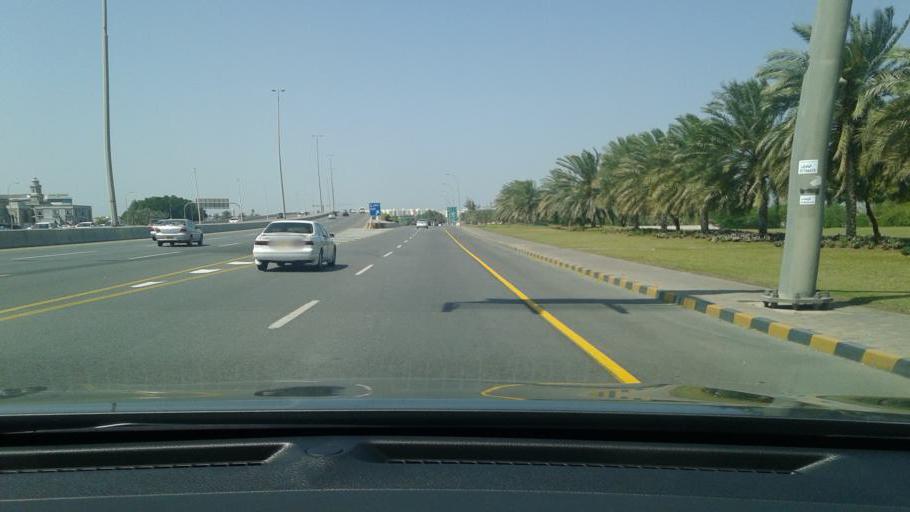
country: OM
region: Muhafazat Masqat
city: As Sib al Jadidah
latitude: 23.6078
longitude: 58.2479
